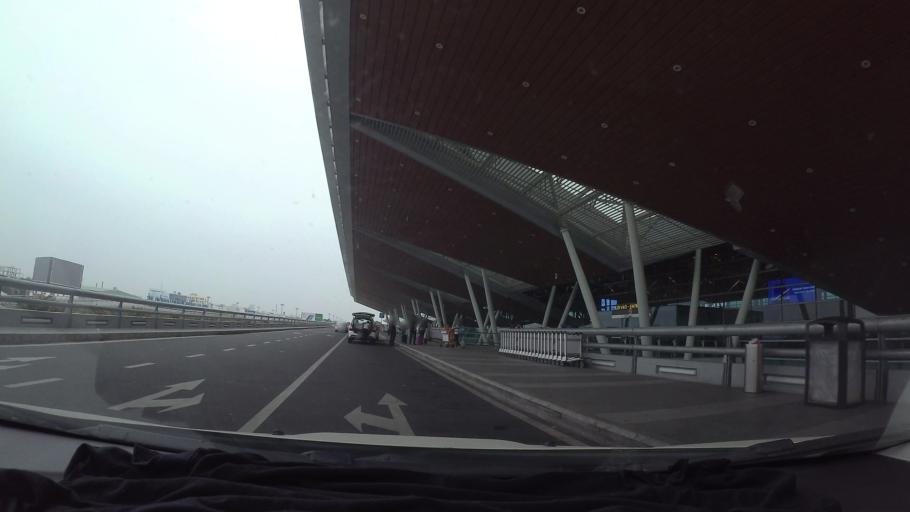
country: VN
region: Da Nang
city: Thanh Khe
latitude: 16.0567
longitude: 108.2028
